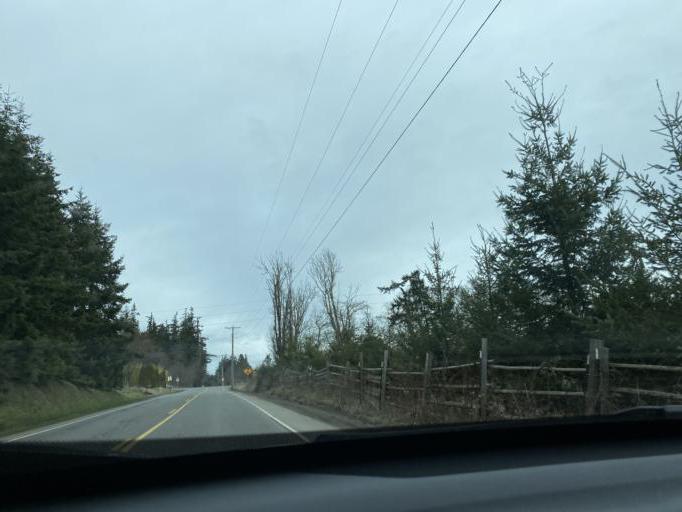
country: US
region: Washington
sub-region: Island County
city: Freeland
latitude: 48.0074
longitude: -122.5069
